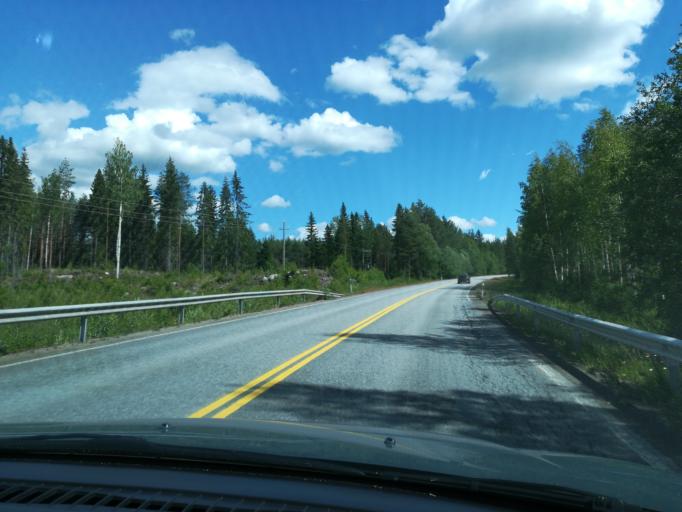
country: FI
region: Southern Savonia
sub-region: Mikkeli
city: Hirvensalmi
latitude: 61.6625
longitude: 26.9612
